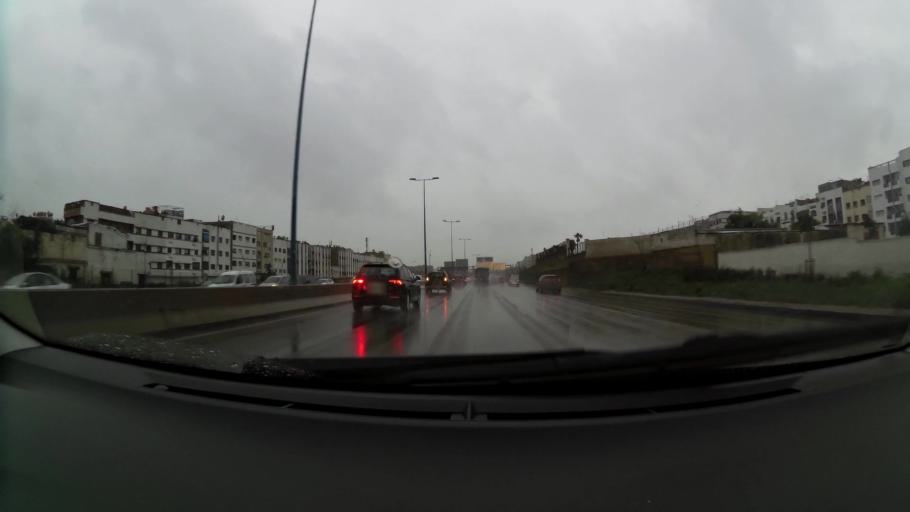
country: MA
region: Grand Casablanca
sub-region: Casablanca
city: Casablanca
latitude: 33.5830
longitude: -7.5474
